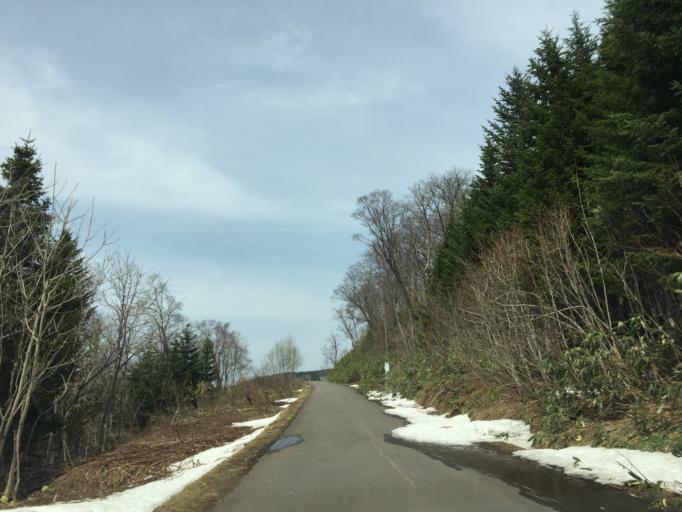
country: JP
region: Hokkaido
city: Akabira
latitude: 43.6028
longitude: 142.0665
